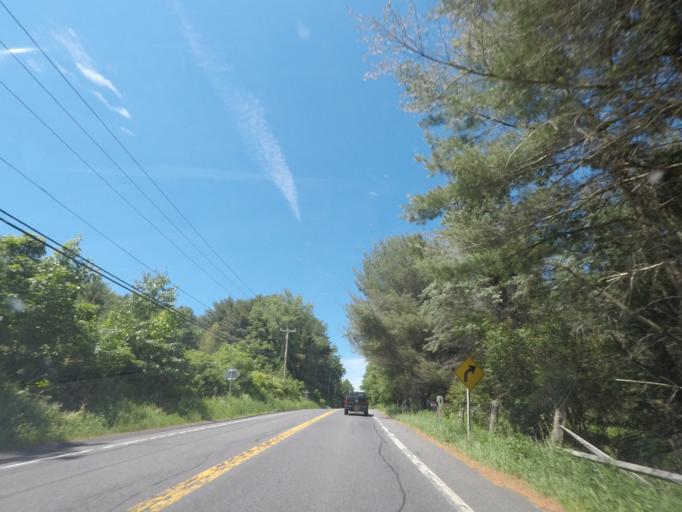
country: US
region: Massachusetts
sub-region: Berkshire County
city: Housatonic
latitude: 42.2203
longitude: -73.5071
